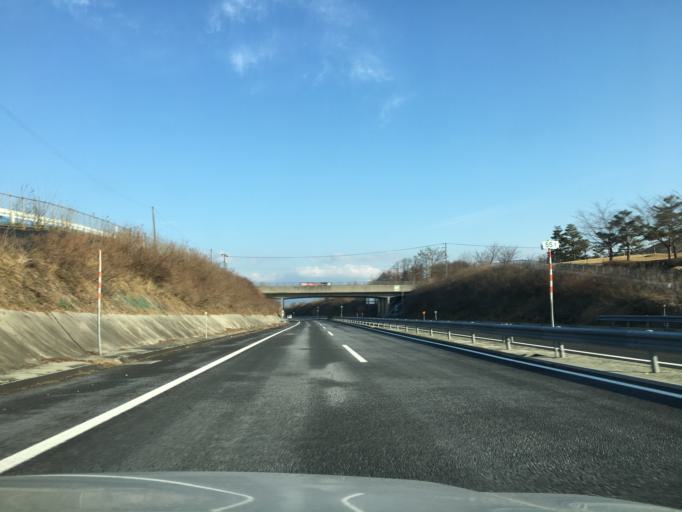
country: JP
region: Yamagata
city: Sagae
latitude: 38.3651
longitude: 140.2662
